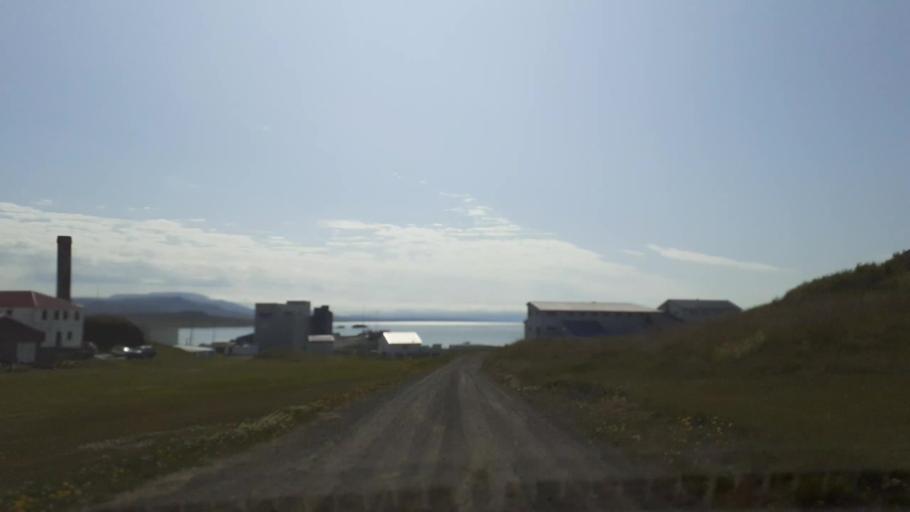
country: IS
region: Northwest
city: Saudarkrokur
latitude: 65.8281
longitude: -20.3208
